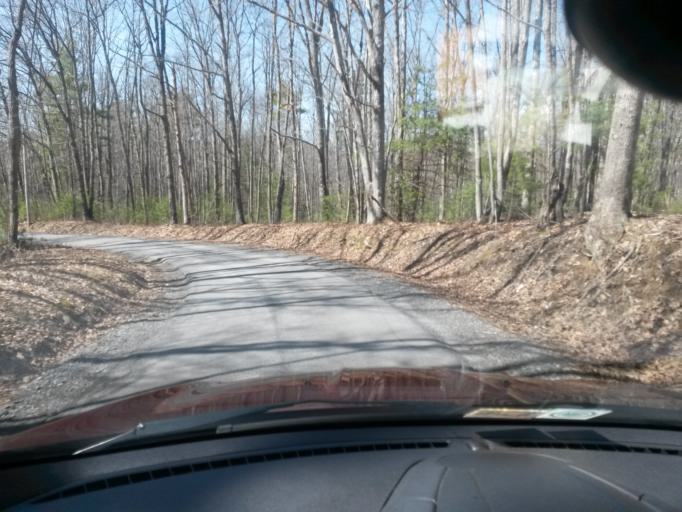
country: US
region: West Virginia
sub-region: Greenbrier County
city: White Sulphur Springs
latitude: 37.6778
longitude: -80.3239
